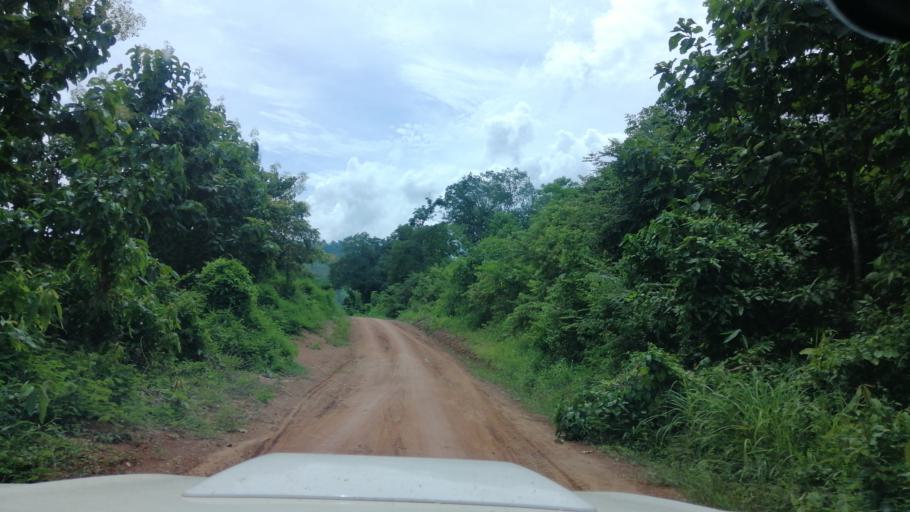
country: TH
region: Nan
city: Bo Kluea
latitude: 18.8969
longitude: 101.4583
